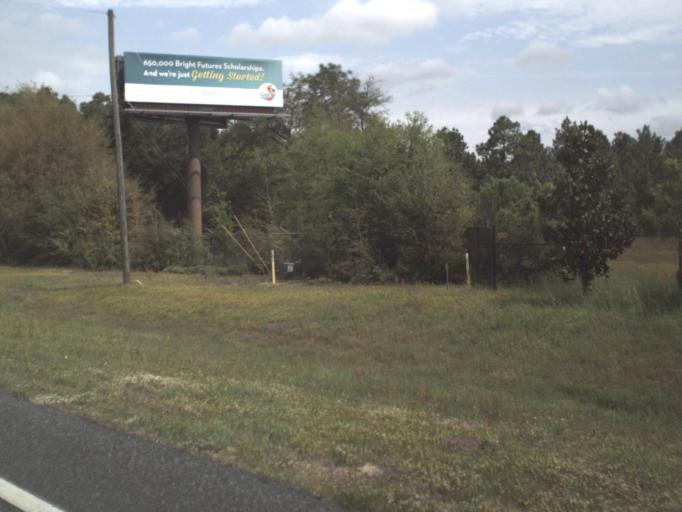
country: US
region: Florida
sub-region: Santa Rosa County
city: East Milton
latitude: 30.5931
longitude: -86.9388
